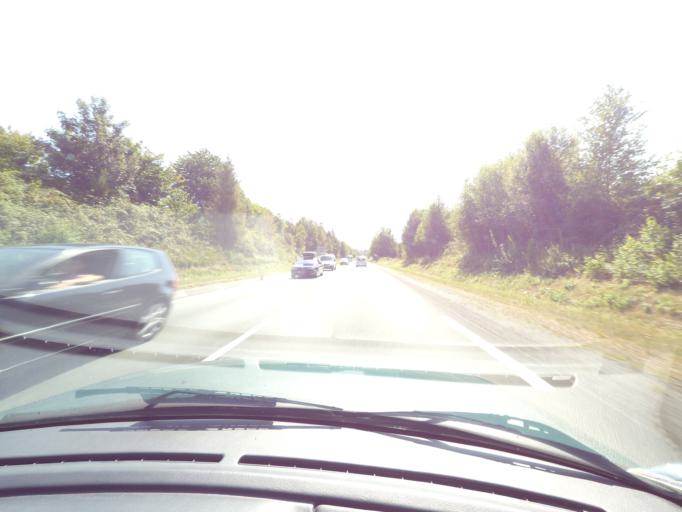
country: FR
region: Limousin
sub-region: Departement de la Haute-Vienne
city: Chaptelat
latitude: 45.9014
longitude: 1.2330
